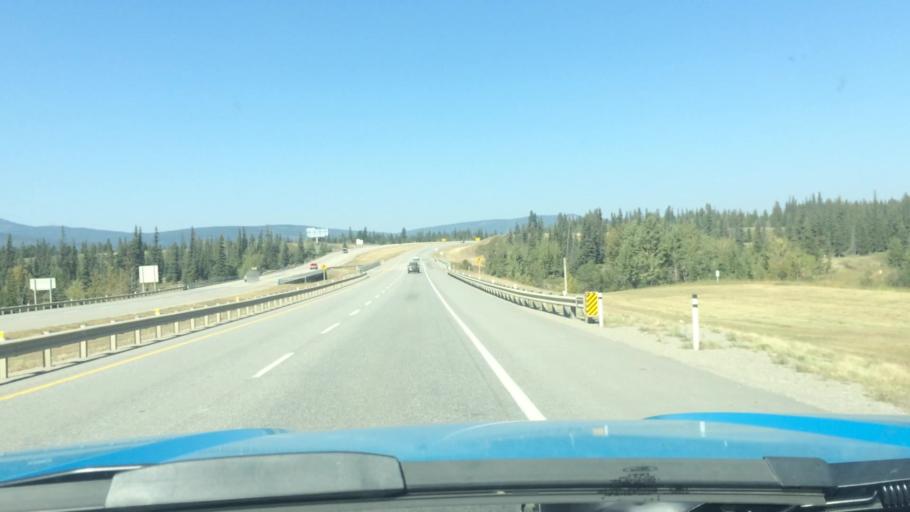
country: CA
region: Alberta
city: Canmore
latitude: 51.0840
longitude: -115.0547
